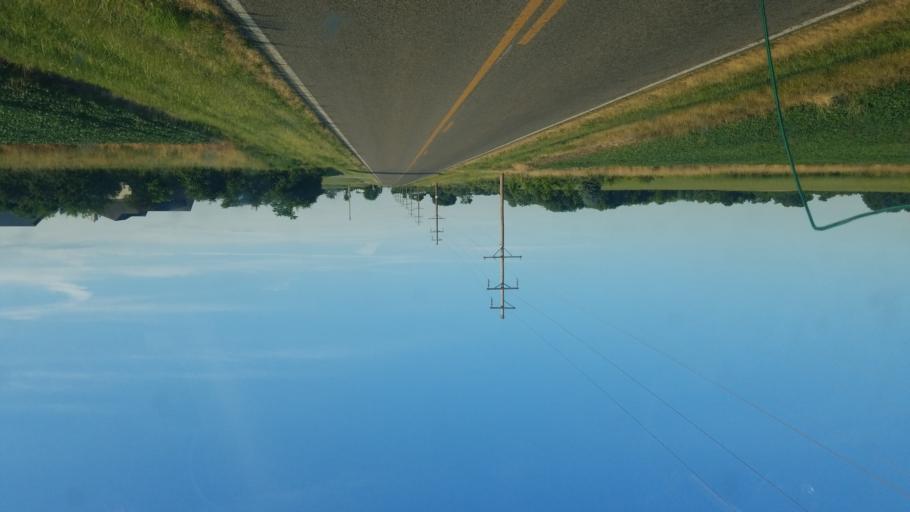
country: US
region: Ohio
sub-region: Williams County
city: Edgerton
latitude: 41.3760
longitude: -84.7671
